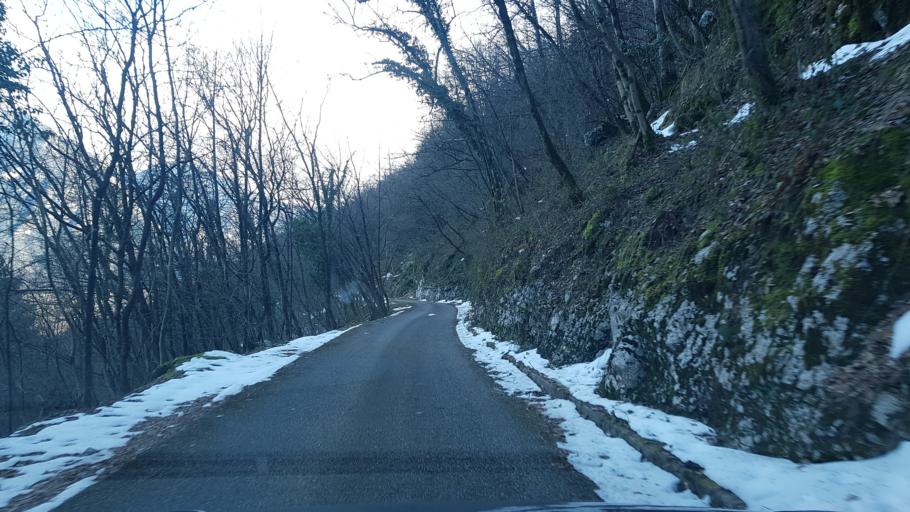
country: IT
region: Friuli Venezia Giulia
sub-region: Provincia di Udine
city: Trasaghis
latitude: 46.2906
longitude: 13.0319
